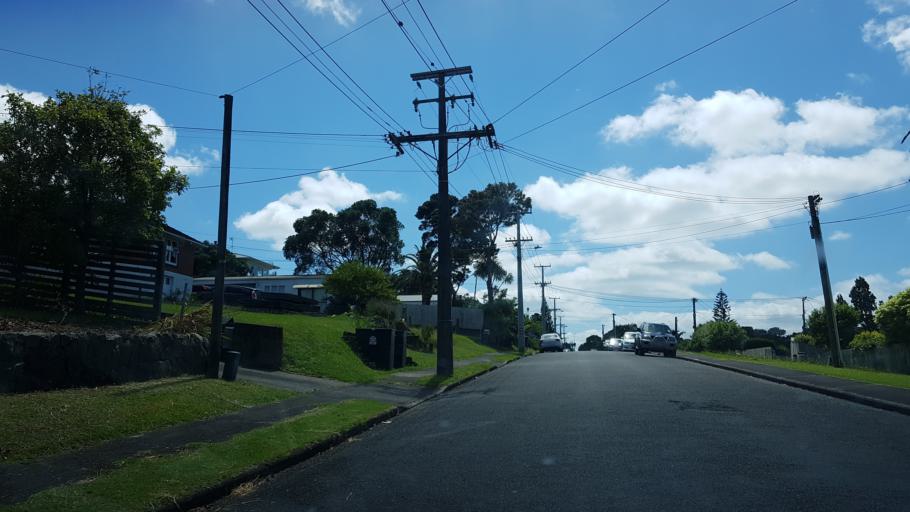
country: NZ
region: Auckland
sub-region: Auckland
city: North Shore
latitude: -36.7921
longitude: 174.7186
